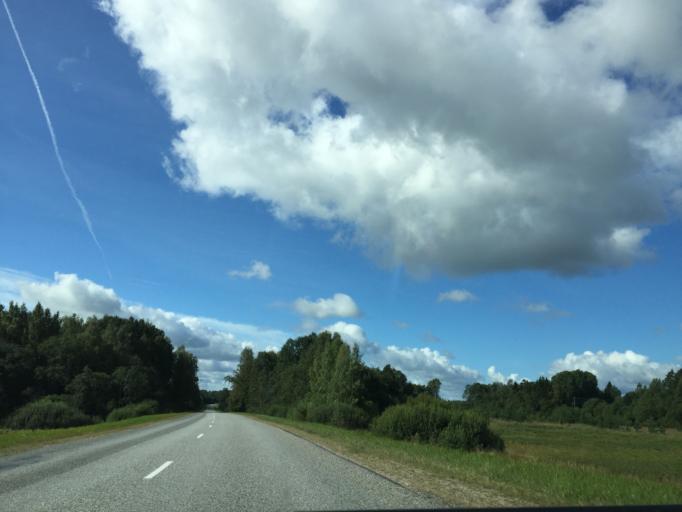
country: LV
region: Kuldigas Rajons
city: Kuldiga
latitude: 56.9917
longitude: 22.0857
